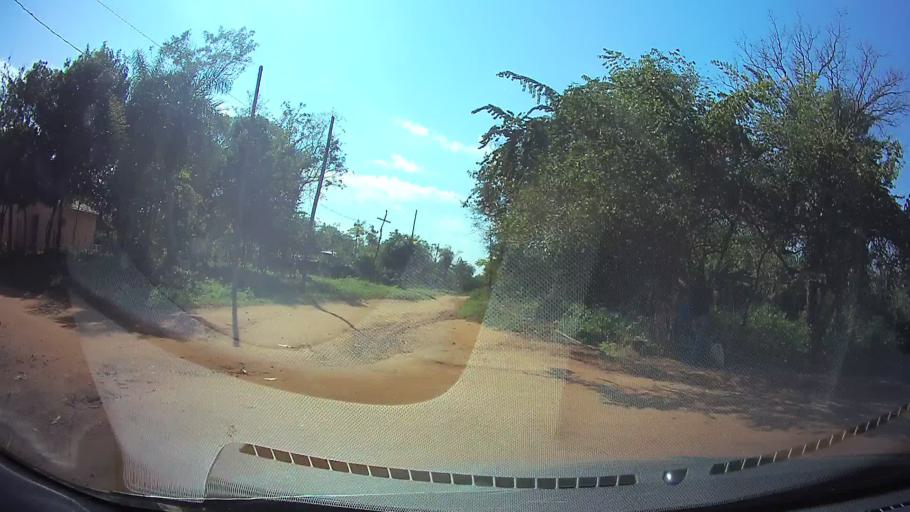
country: PY
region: Central
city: Limpio
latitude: -25.2249
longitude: -57.4359
